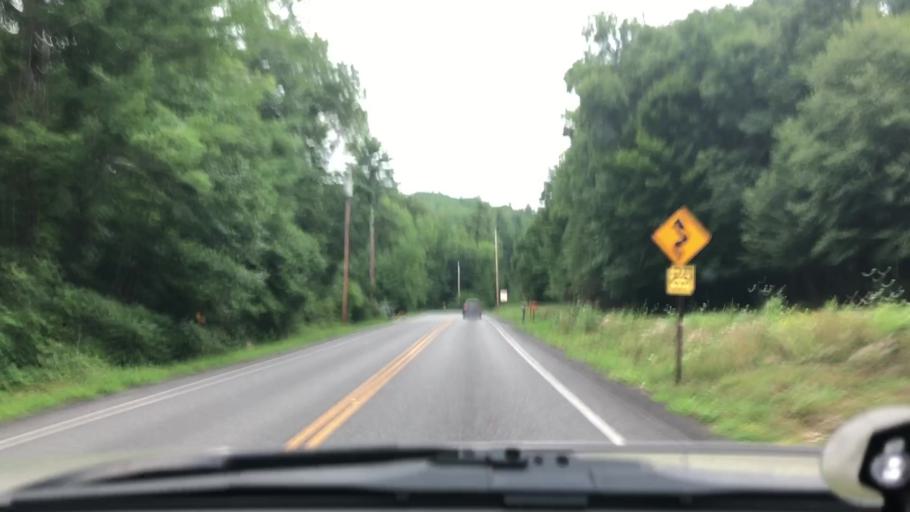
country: US
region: New York
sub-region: Saratoga County
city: Corinth
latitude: 43.1874
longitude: -73.7514
